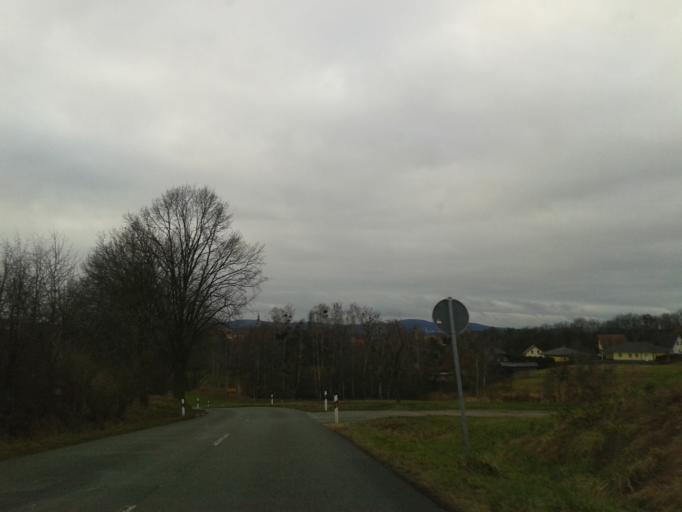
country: DE
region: Saxony
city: Weissenberg
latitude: 51.2017
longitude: 14.6636
